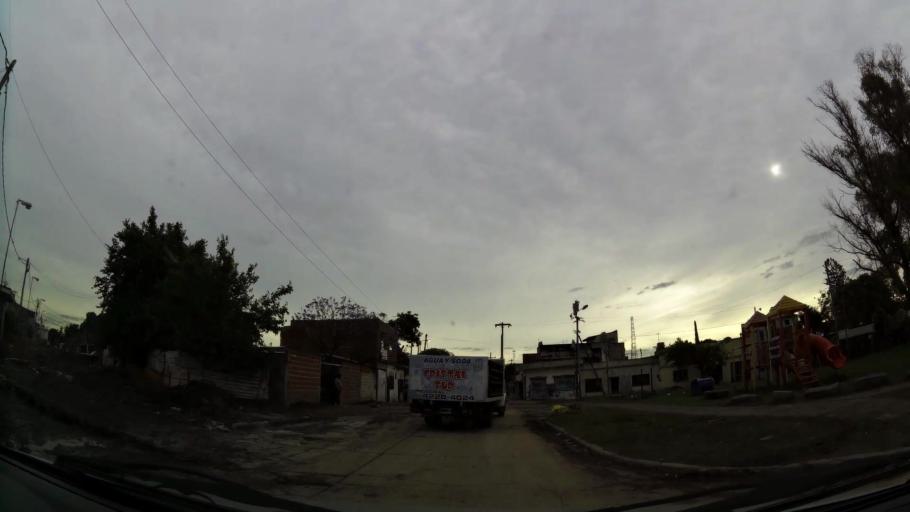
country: AR
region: Buenos Aires
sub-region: Partido de Lanus
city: Lanus
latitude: -34.7232
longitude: -58.3532
